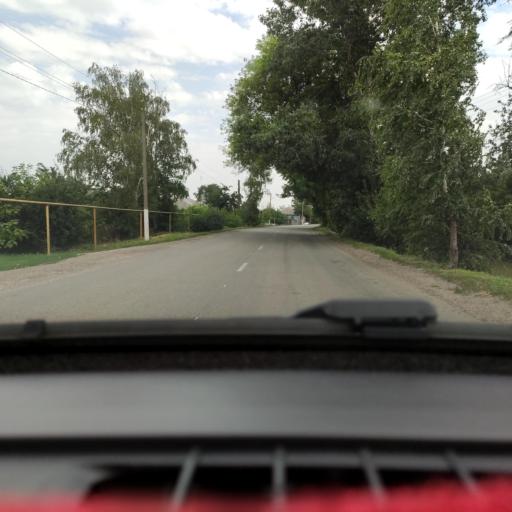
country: RU
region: Voronezj
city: Davydovka
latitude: 51.2173
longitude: 39.5247
